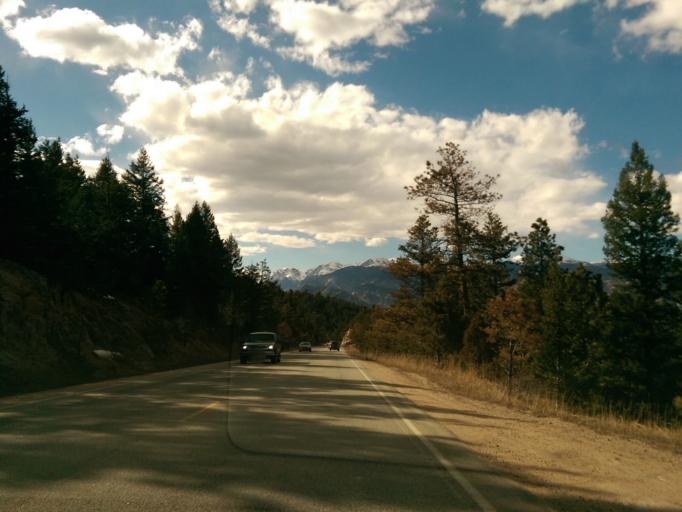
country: US
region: Colorado
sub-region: Larimer County
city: Estes Park
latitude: 40.3616
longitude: -105.4652
